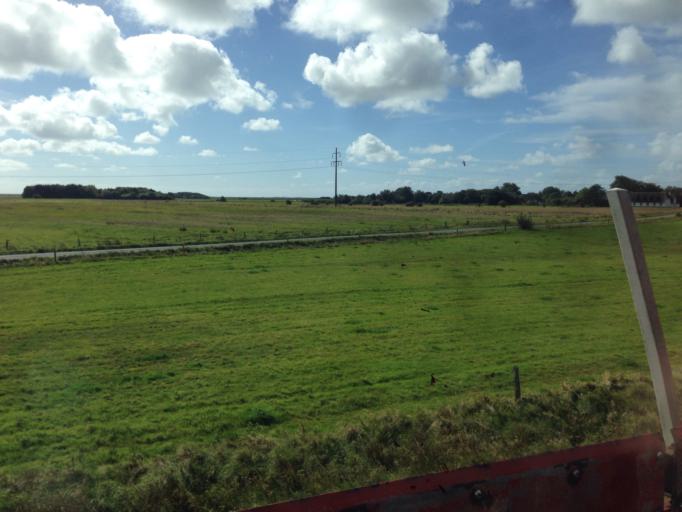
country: DE
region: Schleswig-Holstein
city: Sylt-Ost
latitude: 54.8765
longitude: 8.4073
